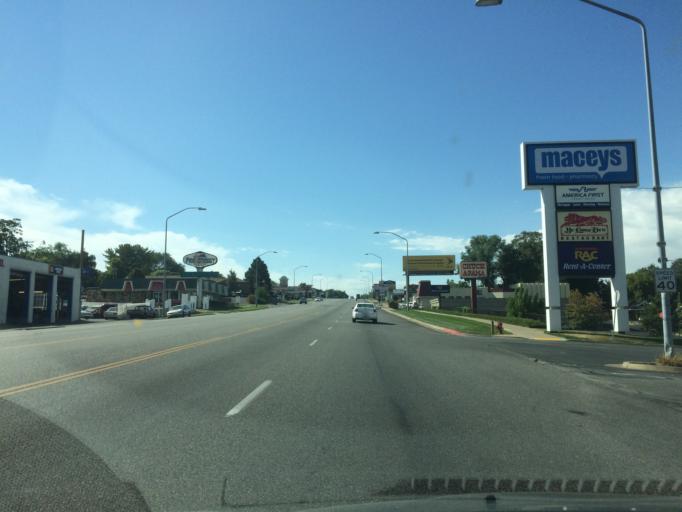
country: US
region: Utah
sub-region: Weber County
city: South Ogden
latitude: 41.1972
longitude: -111.9711
